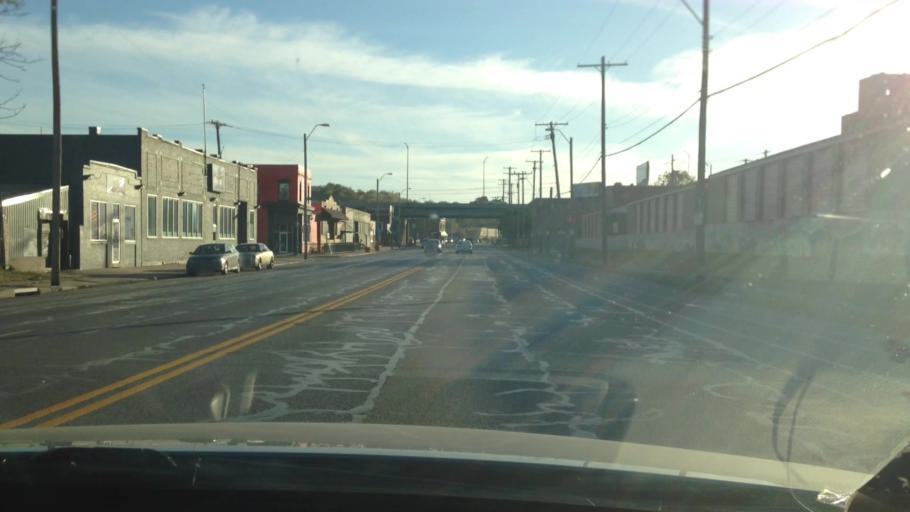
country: US
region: Missouri
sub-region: Jackson County
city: Kansas City
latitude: 39.0778
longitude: -94.6010
